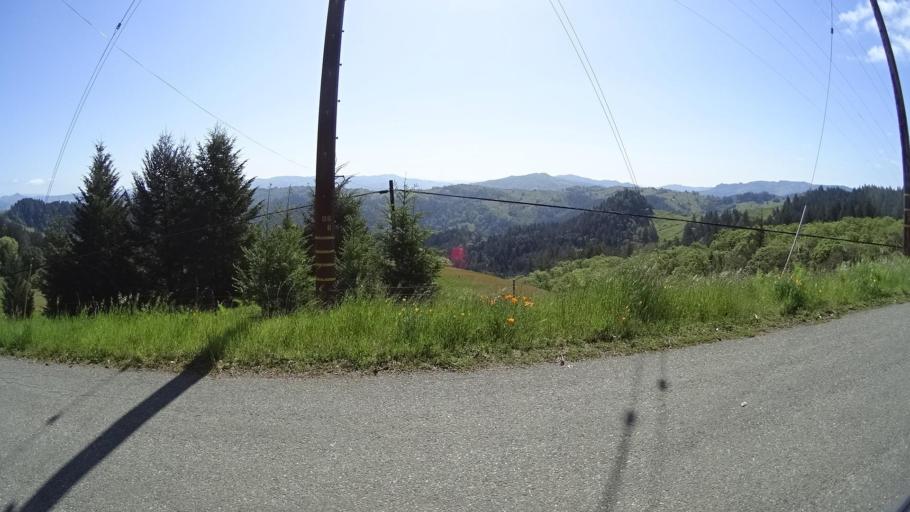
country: US
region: California
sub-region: Humboldt County
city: Redway
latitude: 40.0530
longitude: -123.6399
